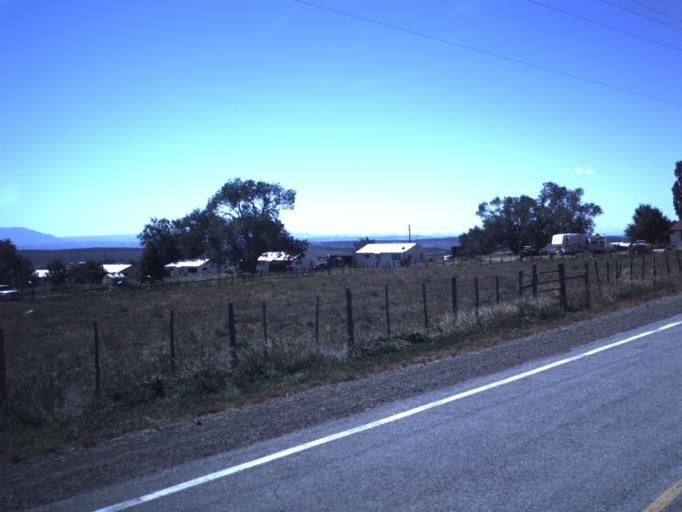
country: US
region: Utah
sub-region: Grand County
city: Moab
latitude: 38.3124
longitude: -109.2495
